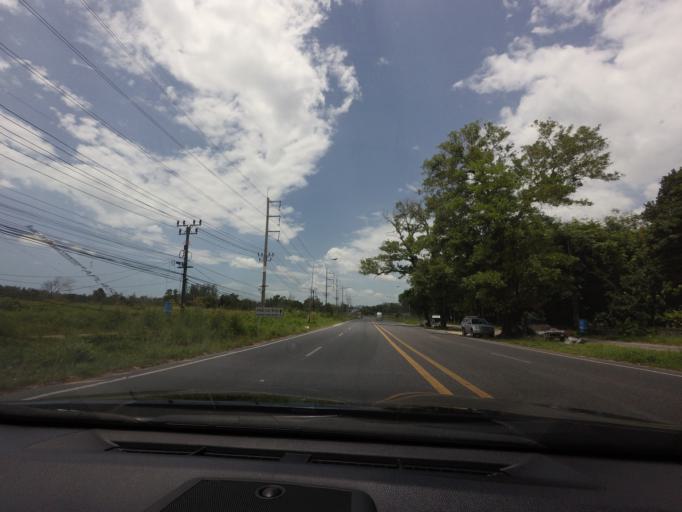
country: TH
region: Phangnga
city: Ban Khao Lak
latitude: 8.6515
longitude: 98.2529
